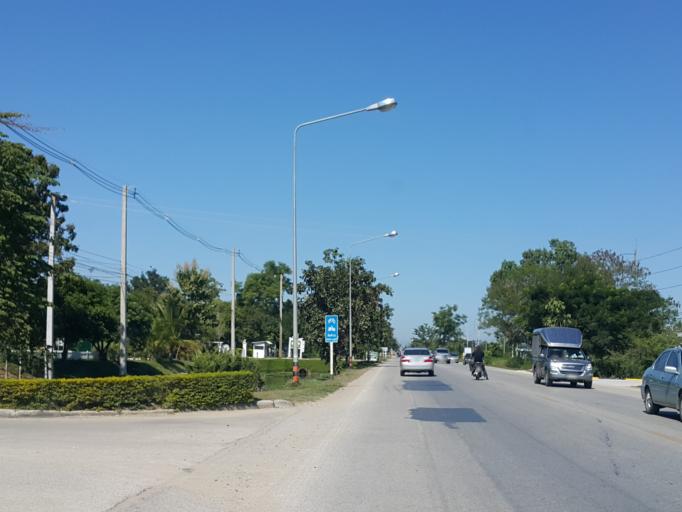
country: TH
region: Chiang Mai
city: San Sai
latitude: 18.7975
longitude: 99.0652
